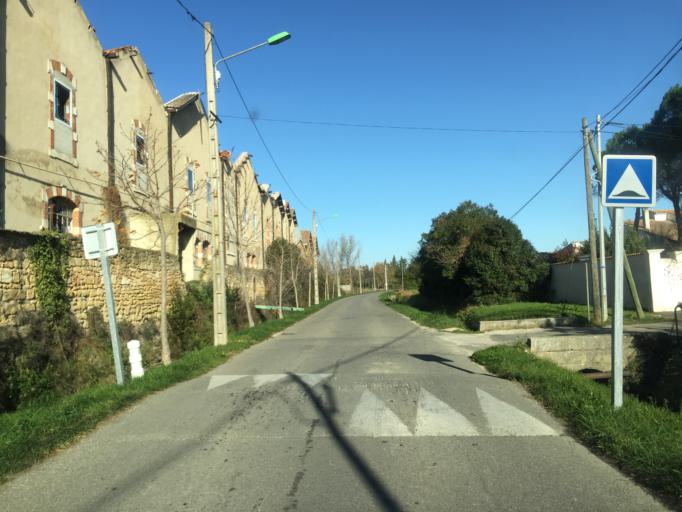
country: FR
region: Provence-Alpes-Cote d'Azur
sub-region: Departement du Vaucluse
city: Bedarrides
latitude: 44.0458
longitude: 4.9004
